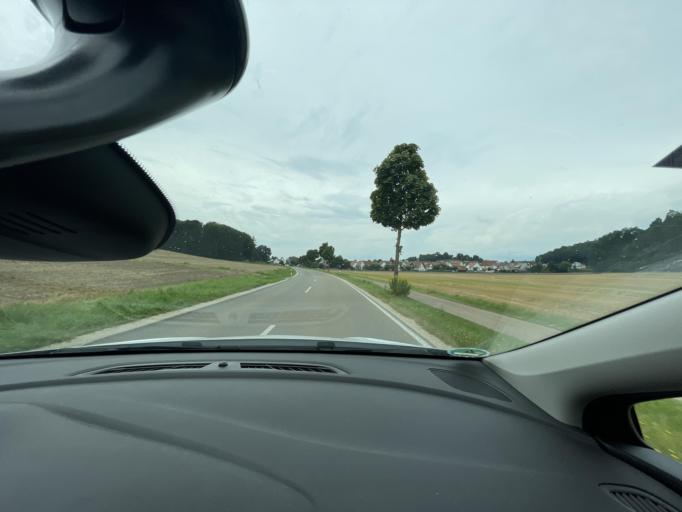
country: DE
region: Bavaria
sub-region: Swabia
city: Thierhaupten
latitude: 48.5633
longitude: 10.9281
